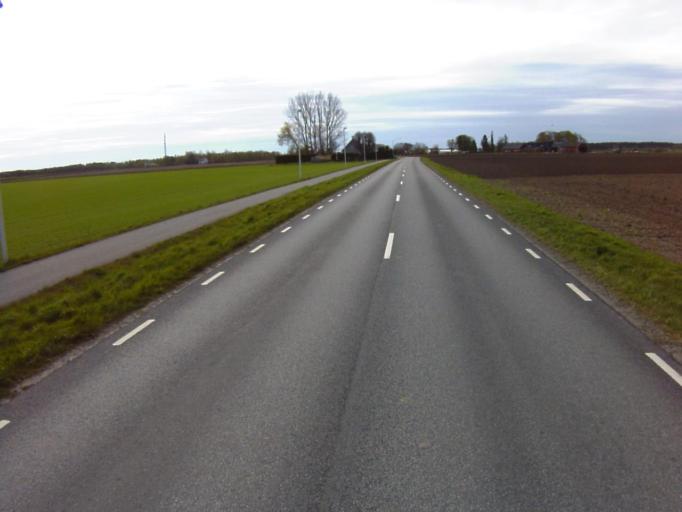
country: SE
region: Skane
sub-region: Kristianstads Kommun
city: Norra Asum
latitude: 56.0073
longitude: 14.1296
